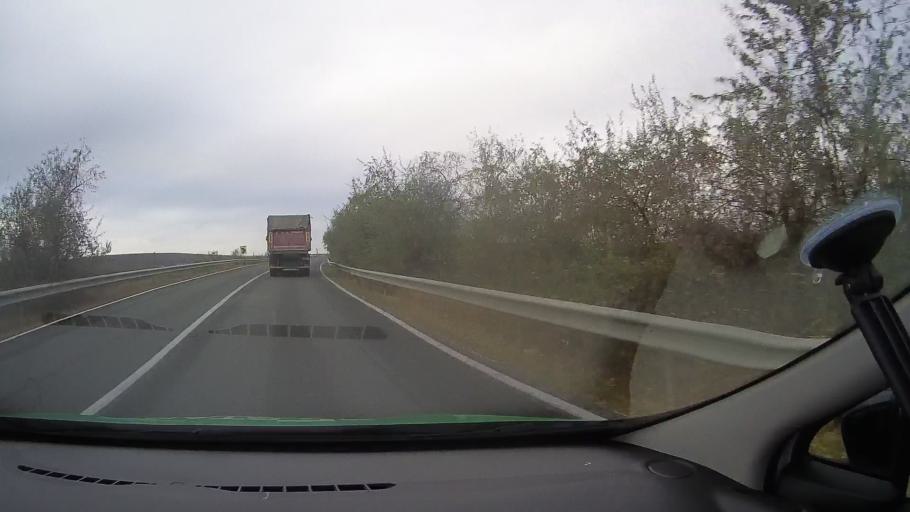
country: RO
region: Constanta
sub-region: Comuna Poarta Alba
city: Poarta Alba
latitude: 44.2147
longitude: 28.3916
